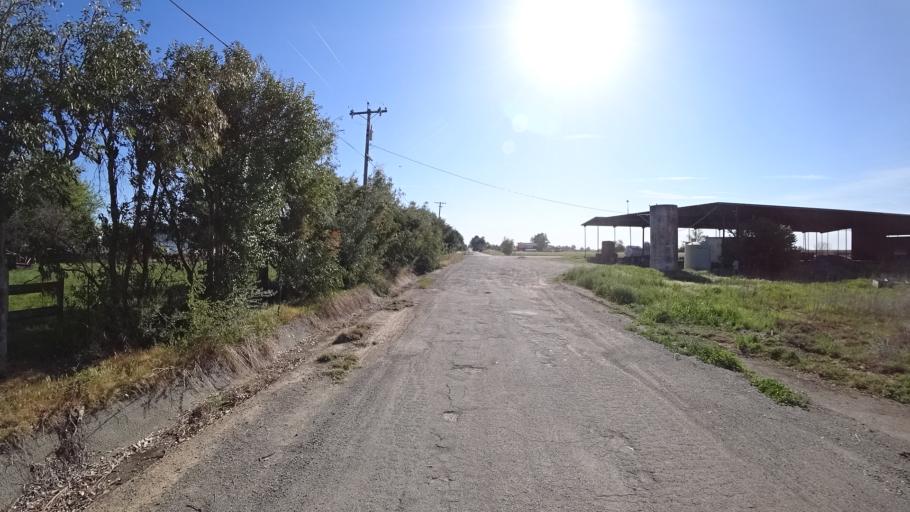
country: US
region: California
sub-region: Glenn County
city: Orland
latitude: 39.7114
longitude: -122.2169
